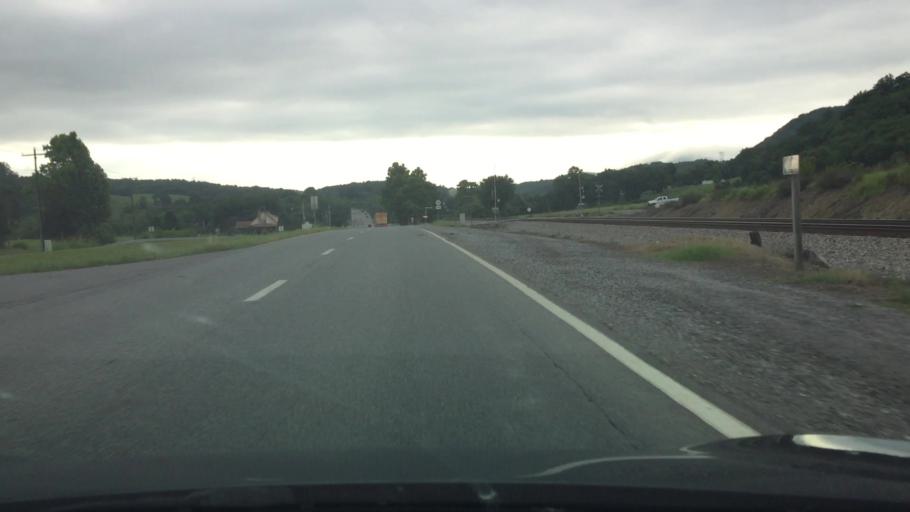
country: US
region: Virginia
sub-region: Montgomery County
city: Shawsville
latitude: 37.2305
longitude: -80.2010
